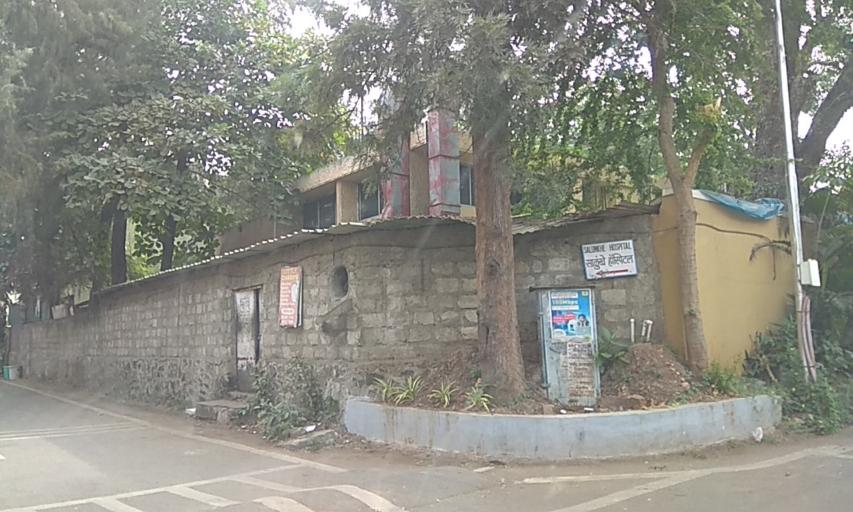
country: IN
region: Maharashtra
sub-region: Pune Division
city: Pune
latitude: 18.5026
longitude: 73.9302
